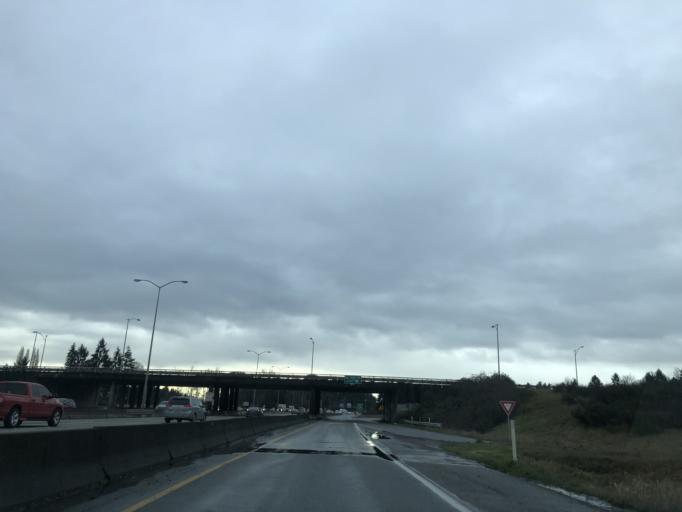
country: US
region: Washington
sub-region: Pierce County
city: Tacoma
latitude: 47.2077
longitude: -122.4623
